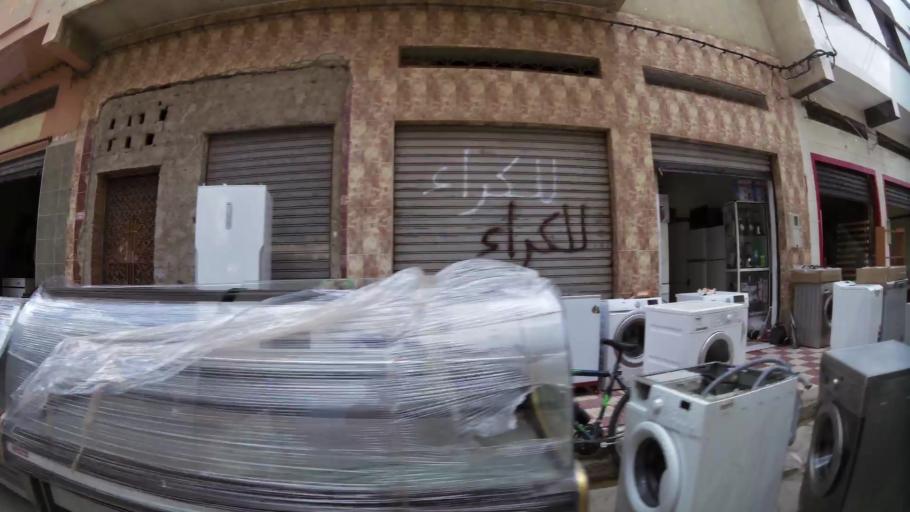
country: MA
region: Oriental
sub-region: Nador
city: Nador
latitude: 35.1744
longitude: -2.9200
